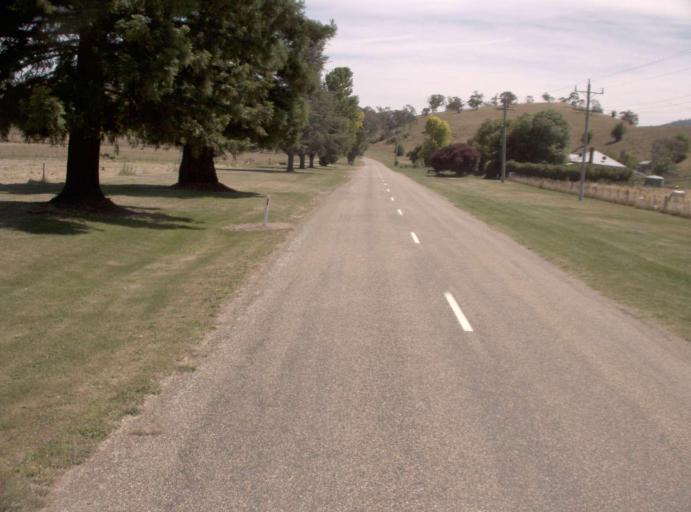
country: AU
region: Victoria
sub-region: Alpine
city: Mount Beauty
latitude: -36.9514
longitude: 147.7032
